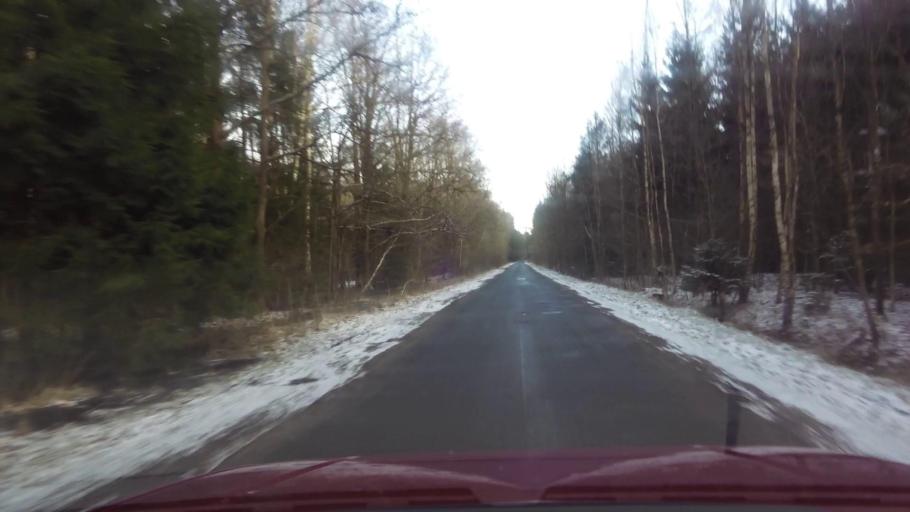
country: PL
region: West Pomeranian Voivodeship
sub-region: Powiat bialogardzki
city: Bialogard
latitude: 54.1062
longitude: 16.0227
